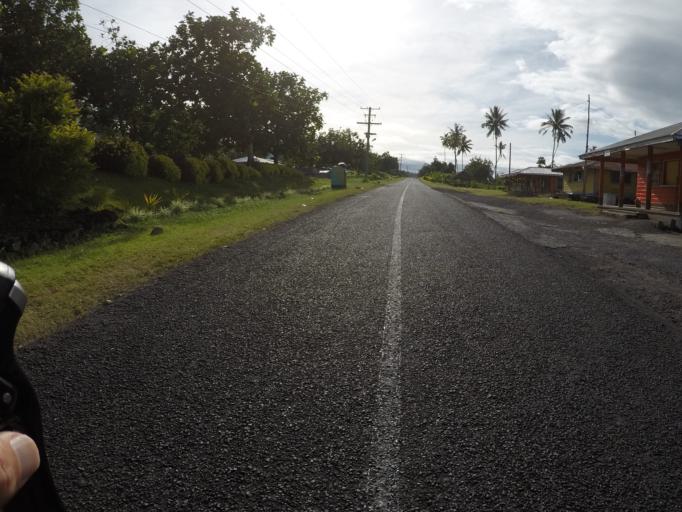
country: WS
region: Vaisigano
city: Asau
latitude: -13.6499
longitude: -172.6588
